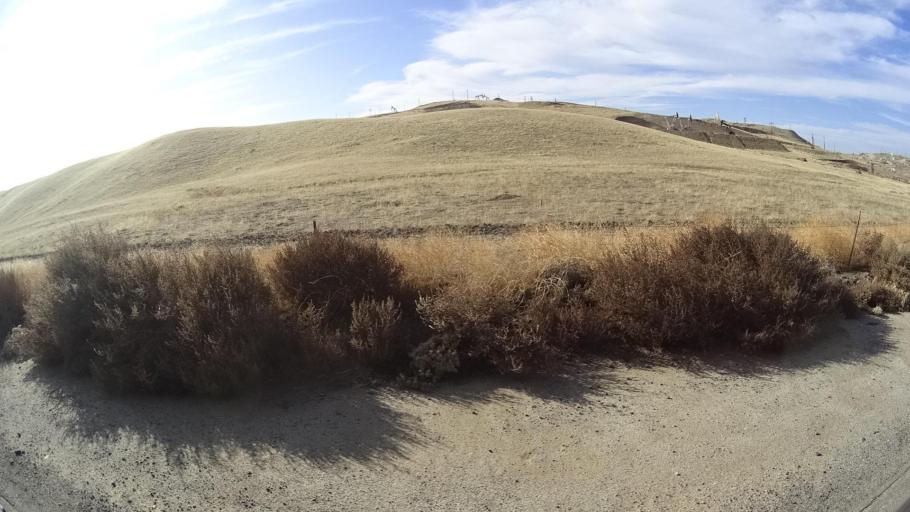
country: US
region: California
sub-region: Kern County
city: Oildale
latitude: 35.6096
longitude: -118.9656
